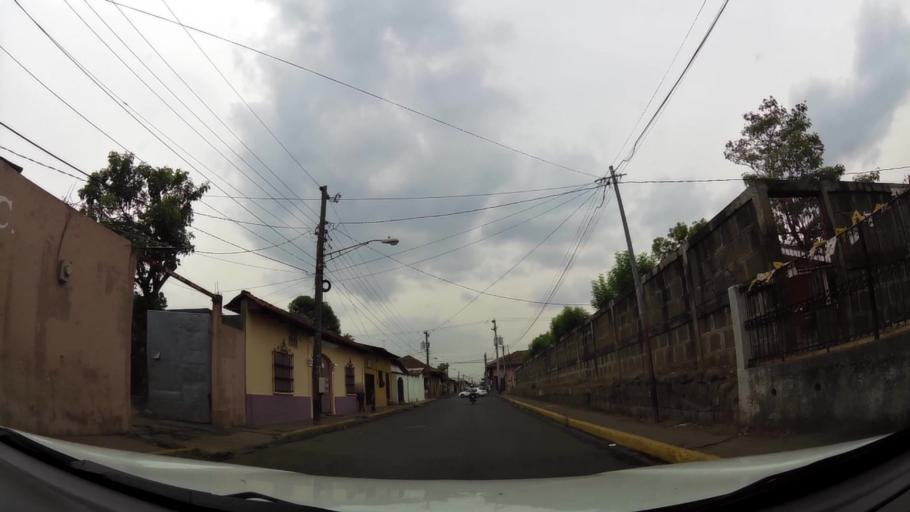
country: NI
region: Leon
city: Leon
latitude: 12.4424
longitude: -86.8802
